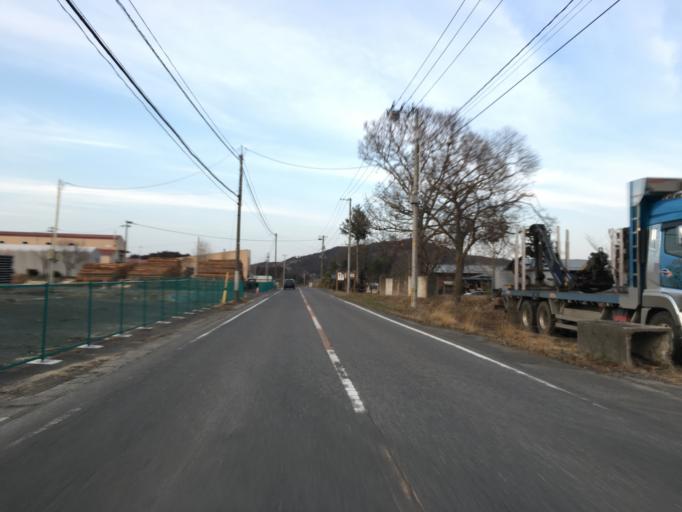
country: JP
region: Ibaraki
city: Daigo
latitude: 36.9416
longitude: 140.4060
